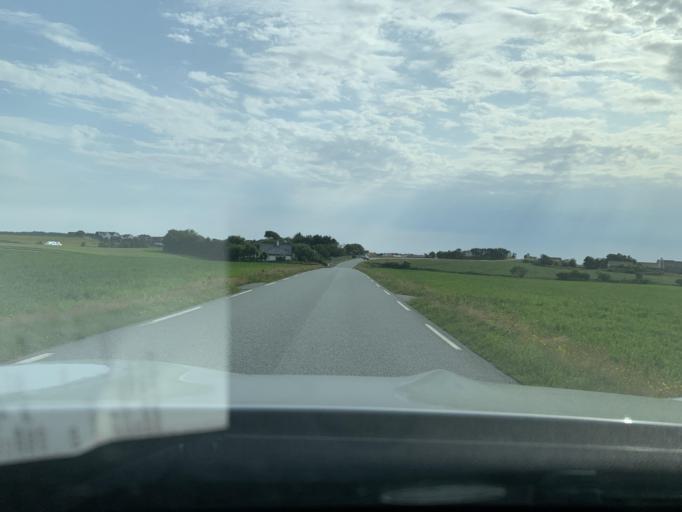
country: NO
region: Rogaland
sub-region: Time
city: Bryne
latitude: 58.7268
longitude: 5.5850
